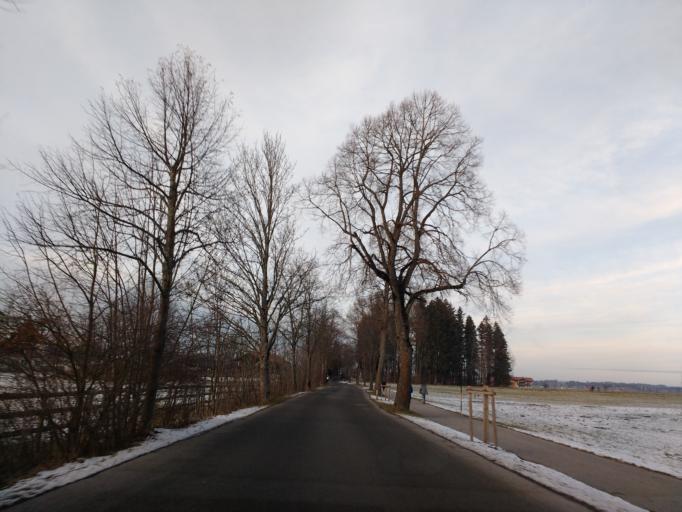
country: DE
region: Bavaria
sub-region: Swabia
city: Schwangau
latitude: 47.5667
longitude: 10.7378
